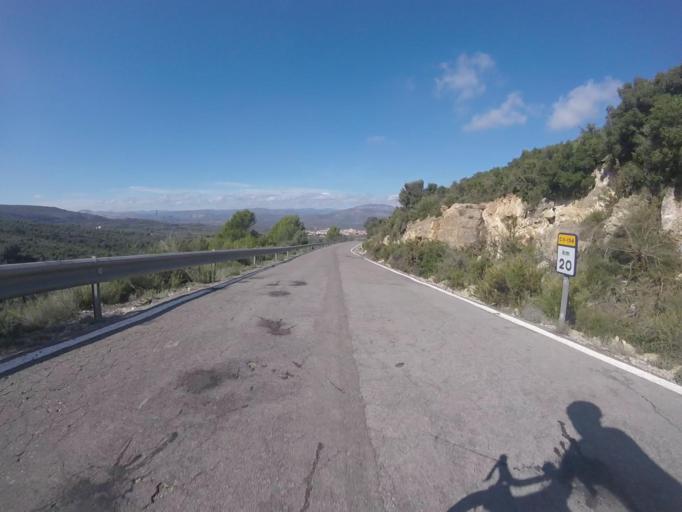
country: ES
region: Valencia
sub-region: Provincia de Castello
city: Albocasser
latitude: 40.3502
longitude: 0.0490
